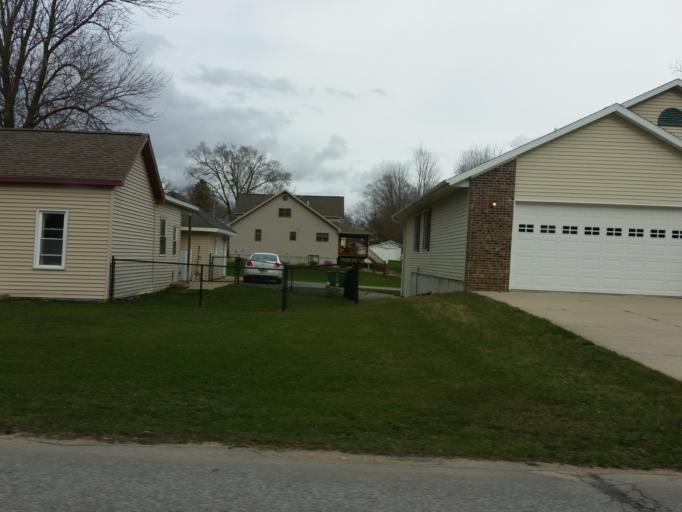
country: US
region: Iowa
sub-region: Black Hawk County
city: Elk Run Heights
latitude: 42.4686
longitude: -92.2199
